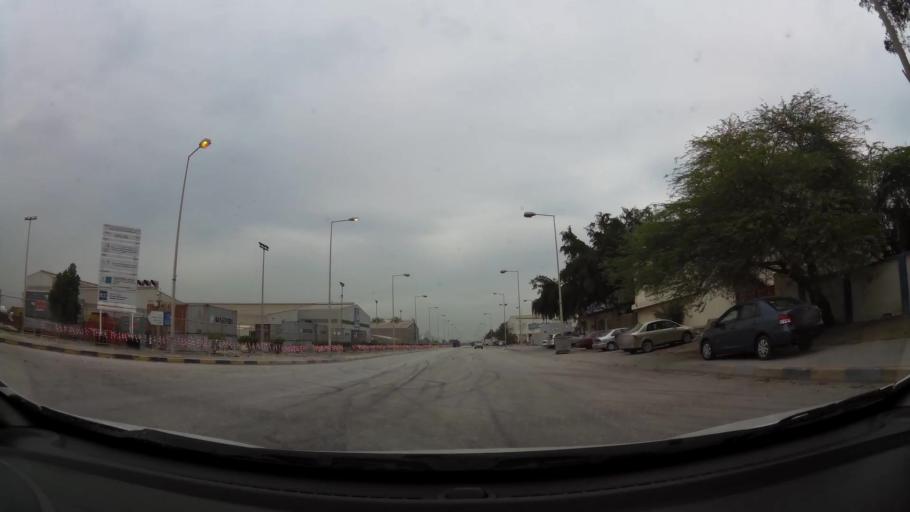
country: BH
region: Northern
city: Sitrah
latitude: 26.1795
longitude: 50.6154
